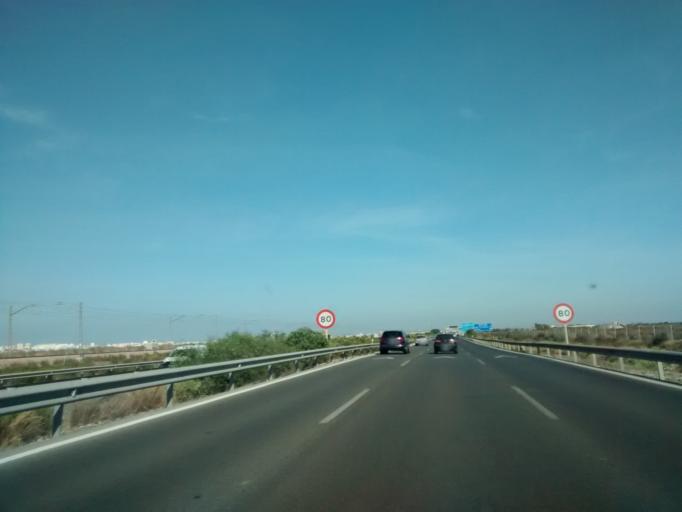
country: ES
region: Andalusia
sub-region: Provincia de Cadiz
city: Chiclana de la Frontera
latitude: 36.4570
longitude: -6.1565
